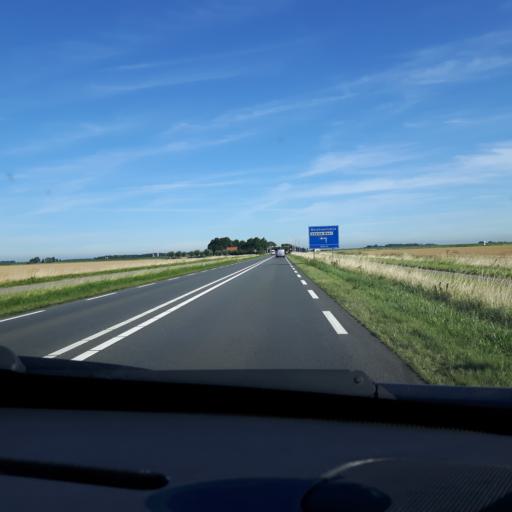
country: NL
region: Zeeland
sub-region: Gemeente Goes
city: Goes
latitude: 51.5258
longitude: 3.8683
